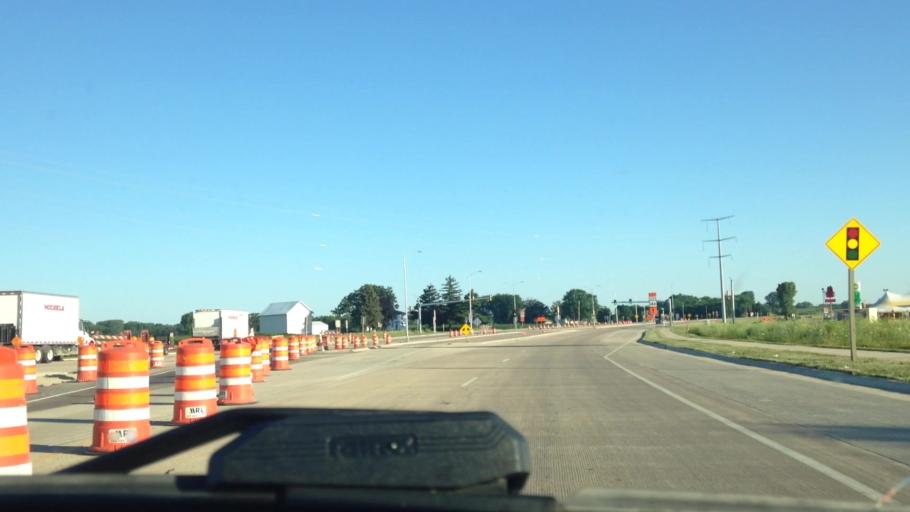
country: US
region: Wisconsin
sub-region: Columbia County
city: Columbus
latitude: 43.3490
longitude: -89.0364
